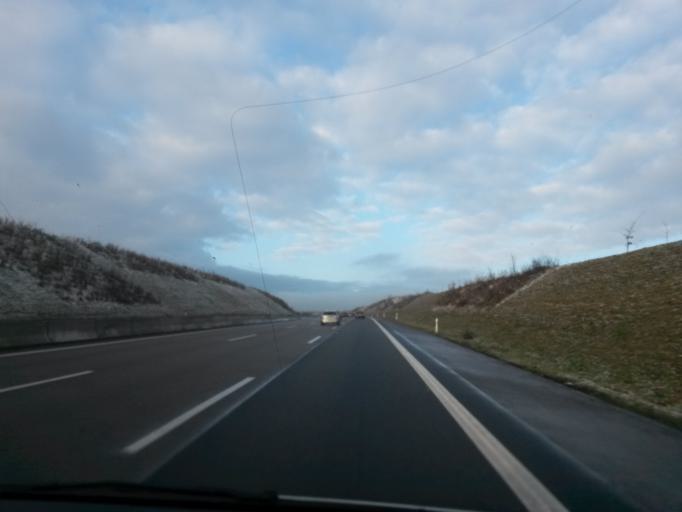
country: DE
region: Baden-Wuerttemberg
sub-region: Regierungsbezirk Stuttgart
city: Rutesheim
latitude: 48.7959
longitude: 8.9596
